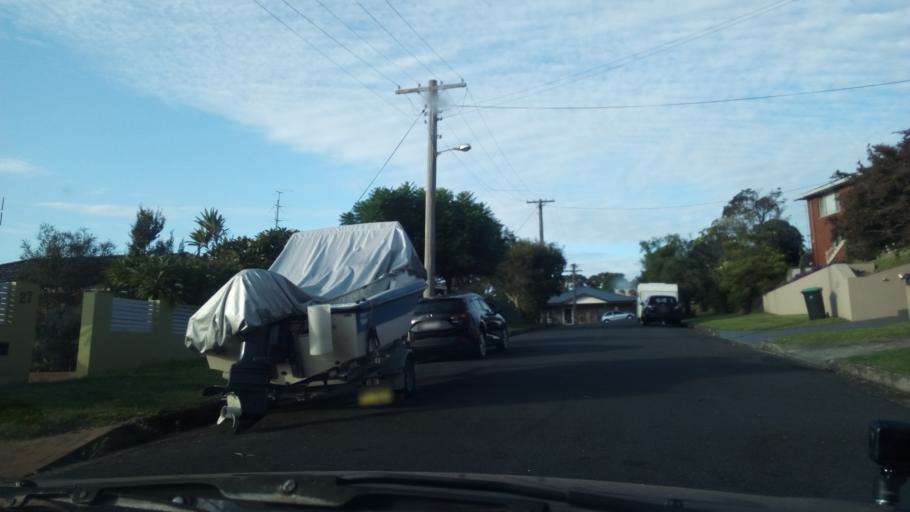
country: AU
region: New South Wales
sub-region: Wollongong
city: Mount Ousley
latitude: -34.3900
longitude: 150.8726
